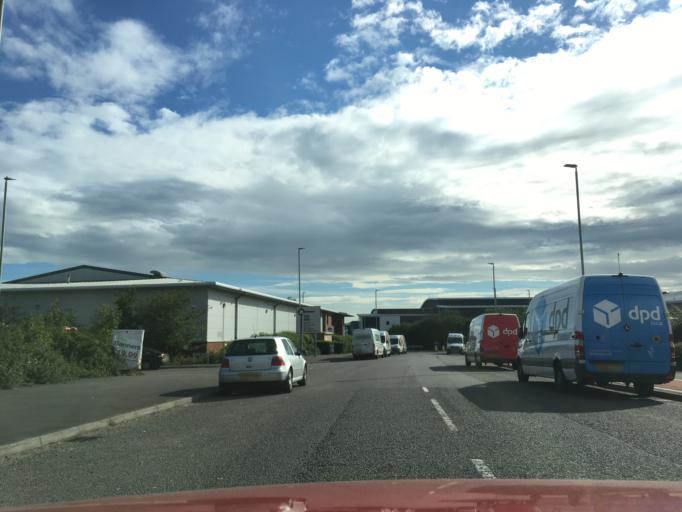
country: GB
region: England
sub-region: Gloucestershire
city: Gloucester
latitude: 51.8128
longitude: -2.2668
